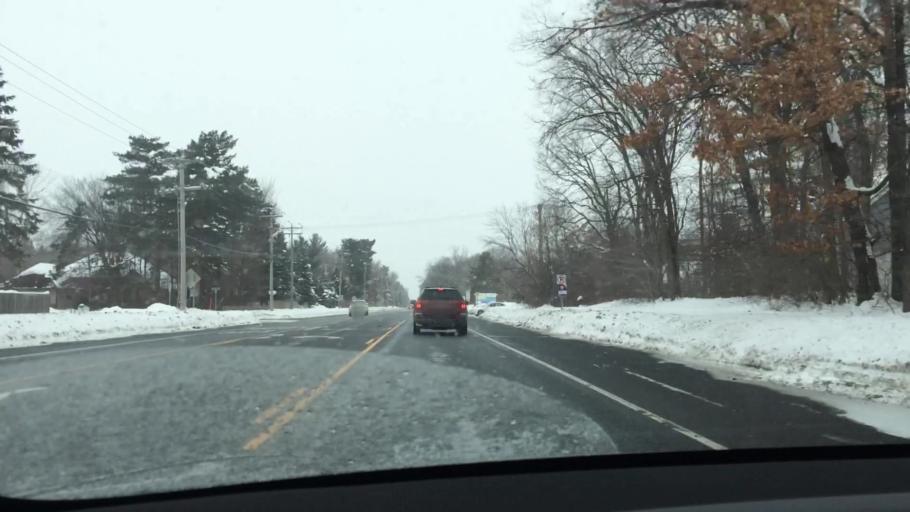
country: US
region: Minnesota
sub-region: Ramsey County
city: Shoreview
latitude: 45.0931
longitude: -93.1271
